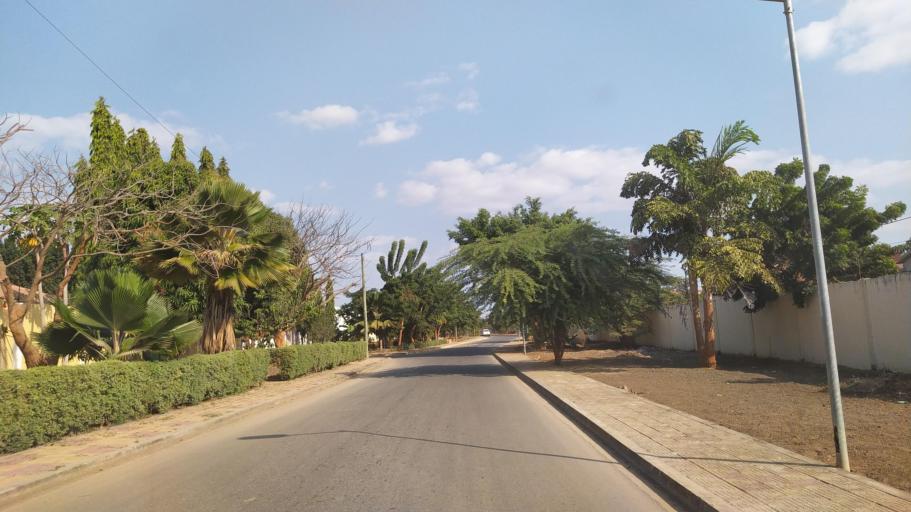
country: AO
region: Luanda
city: Luanda
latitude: -8.8917
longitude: 13.2572
